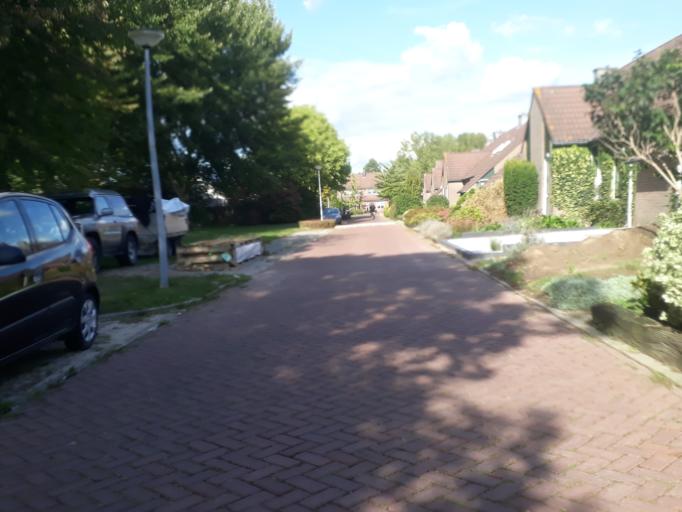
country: NL
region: Gelderland
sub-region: Gemeente Zevenaar
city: Zevenaar
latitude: 51.9319
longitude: 6.0524
